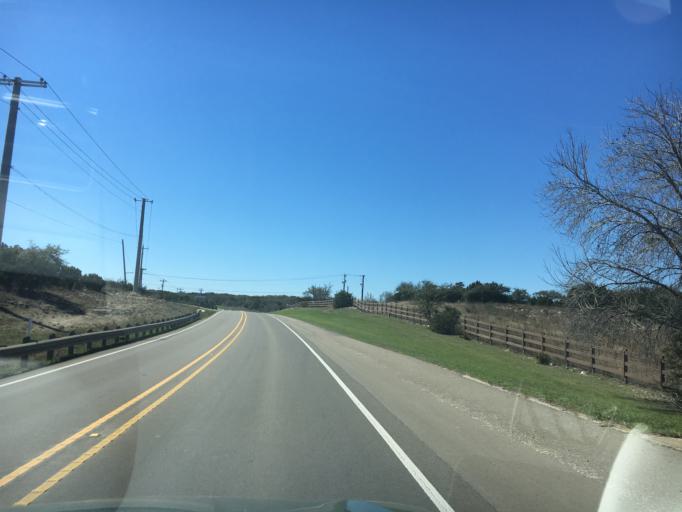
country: US
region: Texas
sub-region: Travis County
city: The Hills
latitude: 30.2915
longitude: -98.0418
